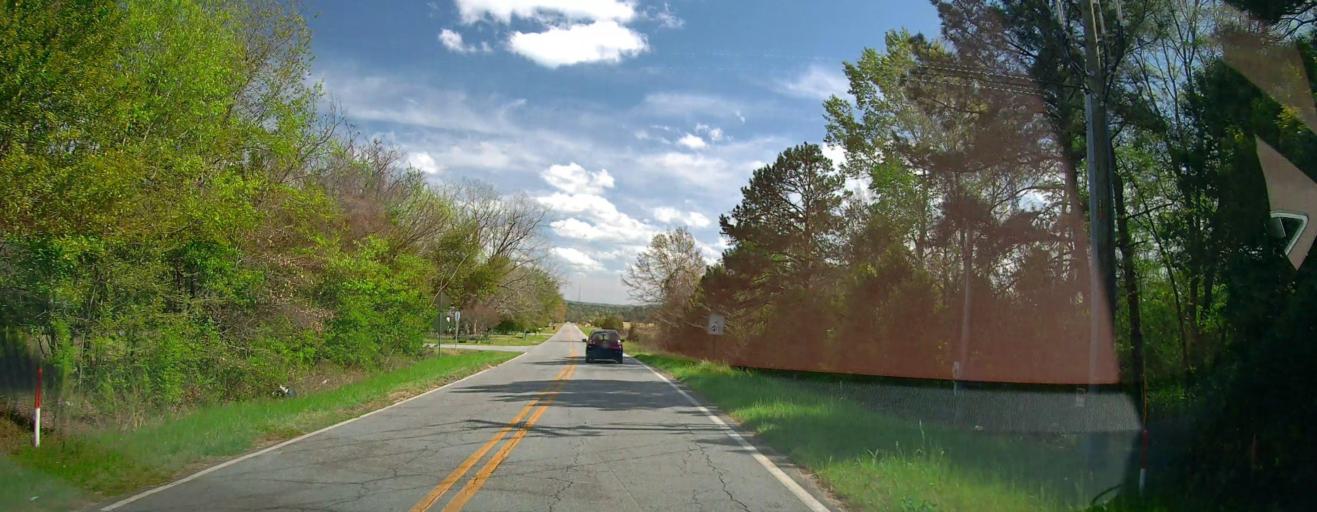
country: US
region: Georgia
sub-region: Bibb County
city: Macon
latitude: 32.8286
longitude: -83.5614
